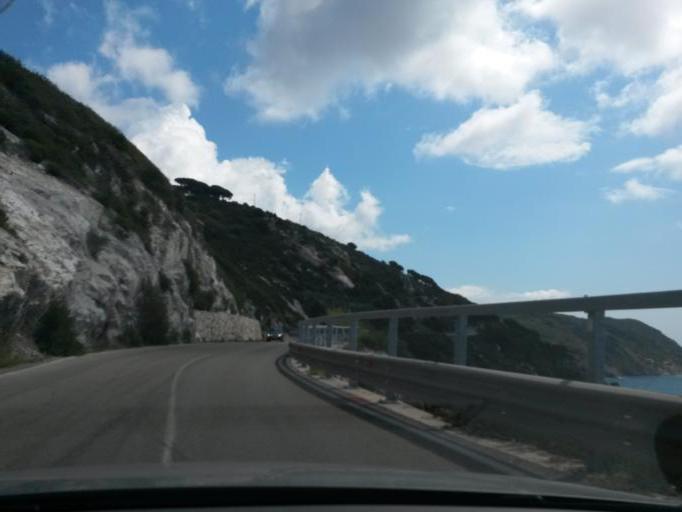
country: IT
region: Tuscany
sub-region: Provincia di Livorno
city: Marina di Campo
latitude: 42.7358
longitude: 10.1912
